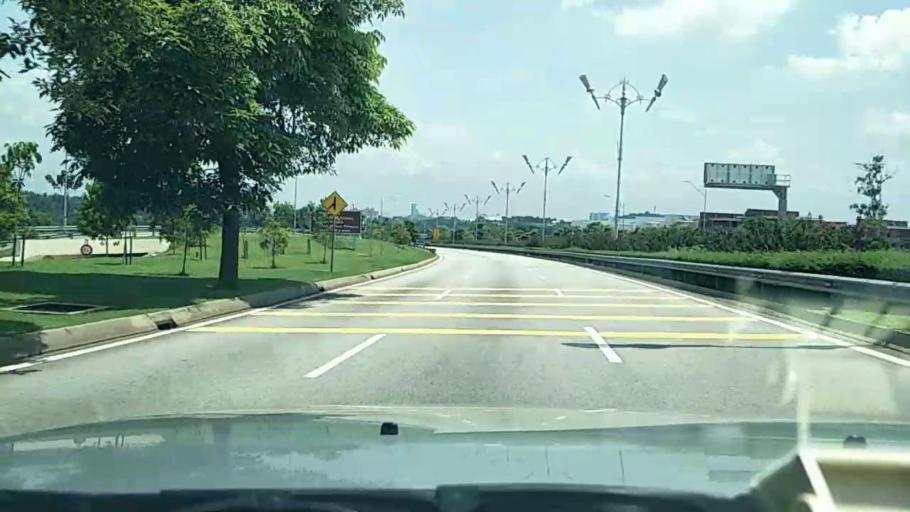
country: MY
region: Putrajaya
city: Putrajaya
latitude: 2.9567
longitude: 101.7045
